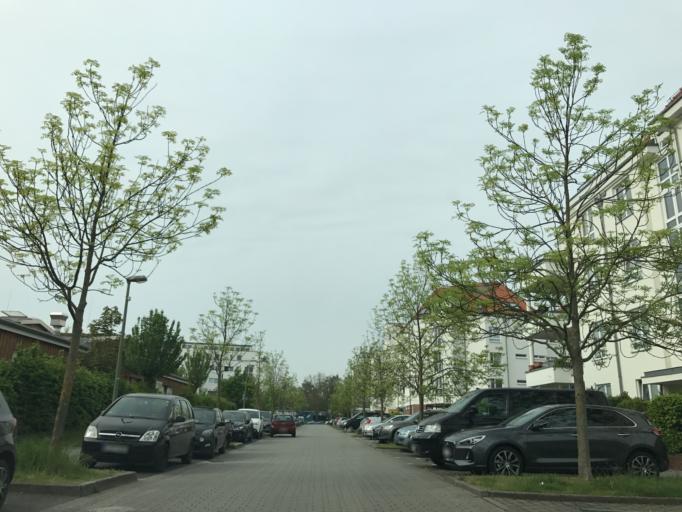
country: DE
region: Berlin
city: Staaken
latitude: 52.5250
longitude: 13.1489
